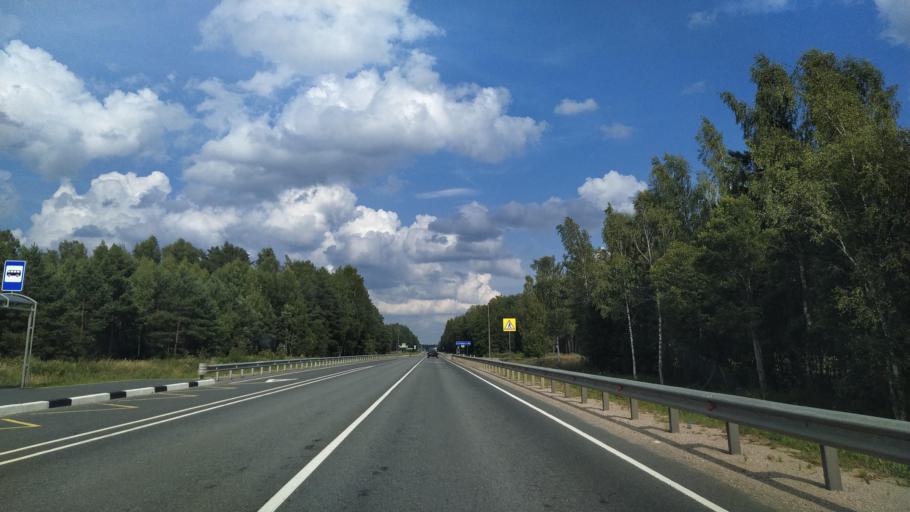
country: RU
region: Novgorod
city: Sol'tsy
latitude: 58.1705
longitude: 30.4925
